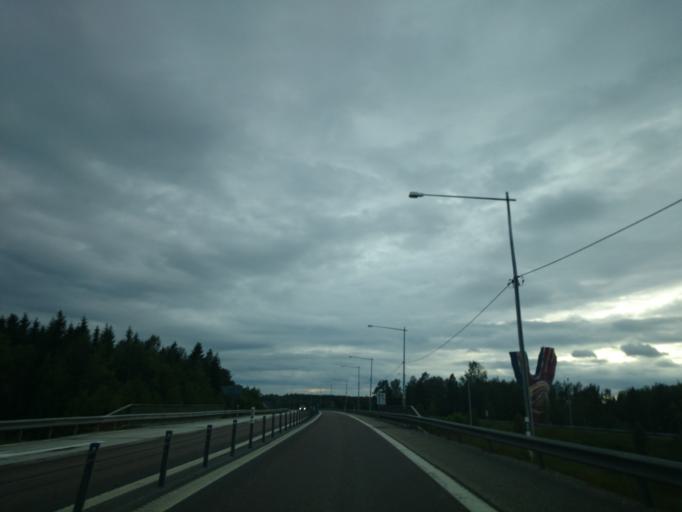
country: SE
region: Vaesternorrland
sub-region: Timra Kommun
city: Bergeforsen
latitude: 62.5182
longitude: 17.4367
